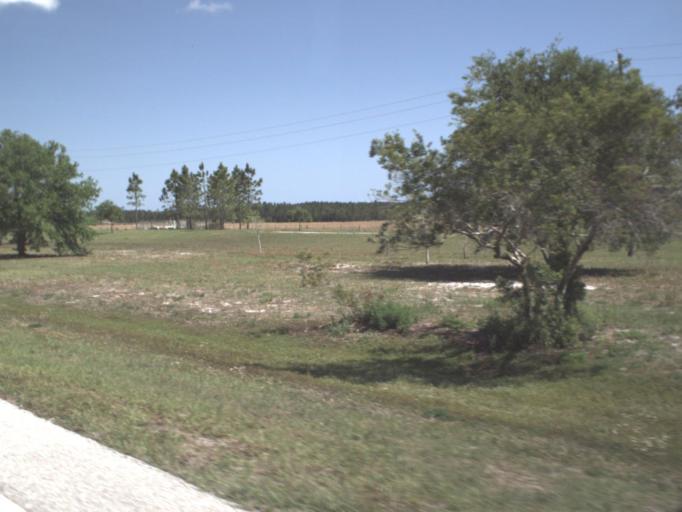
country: US
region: Florida
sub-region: Flagler County
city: Palm Coast
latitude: 29.5711
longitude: -81.2738
